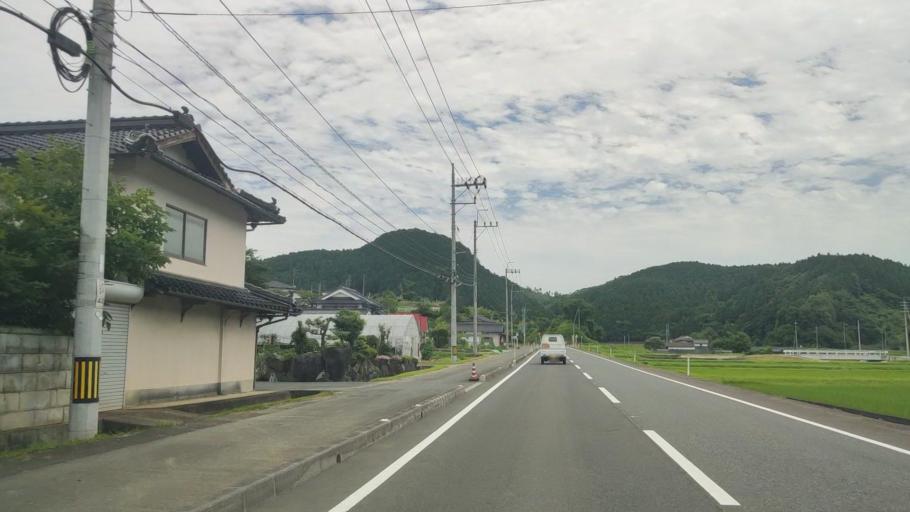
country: JP
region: Okayama
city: Tsuyama
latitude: 35.0630
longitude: 134.2110
